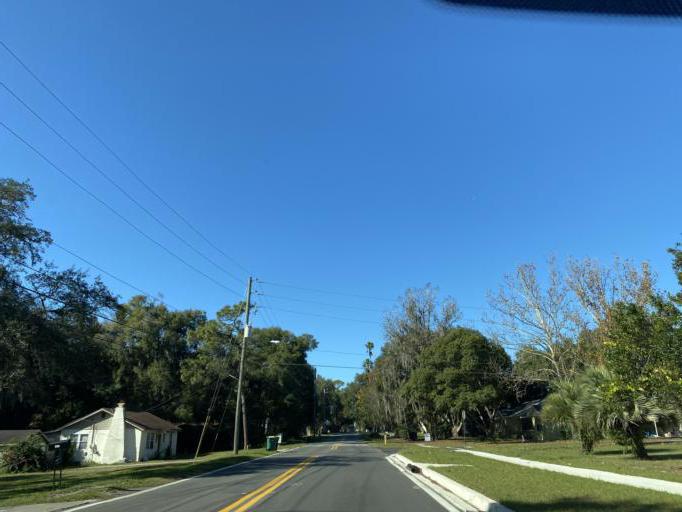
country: US
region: Florida
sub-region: Lake County
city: Mount Dora
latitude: 28.7969
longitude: -81.6279
